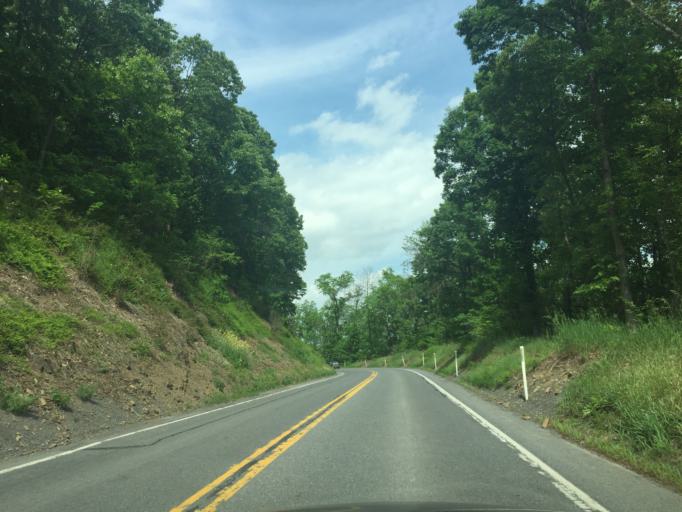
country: US
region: Pennsylvania
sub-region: Fulton County
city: McConnellsburg
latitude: 39.8407
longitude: -78.0788
